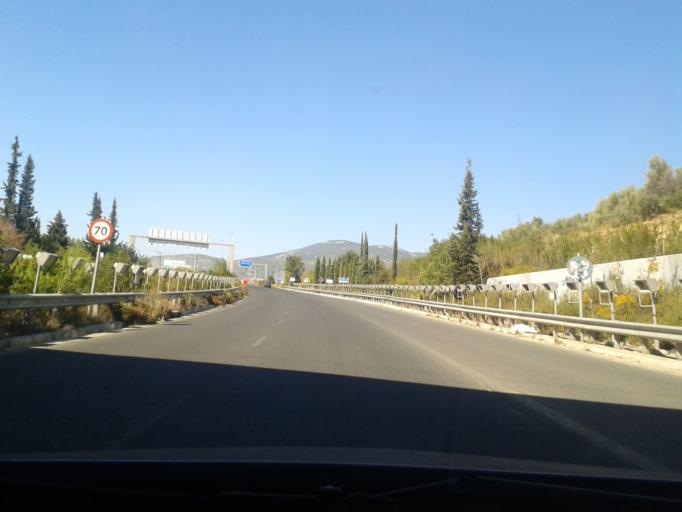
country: GR
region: Attica
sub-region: Nomarchia Athinas
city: Lykovrysi
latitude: 38.0962
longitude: 23.7747
